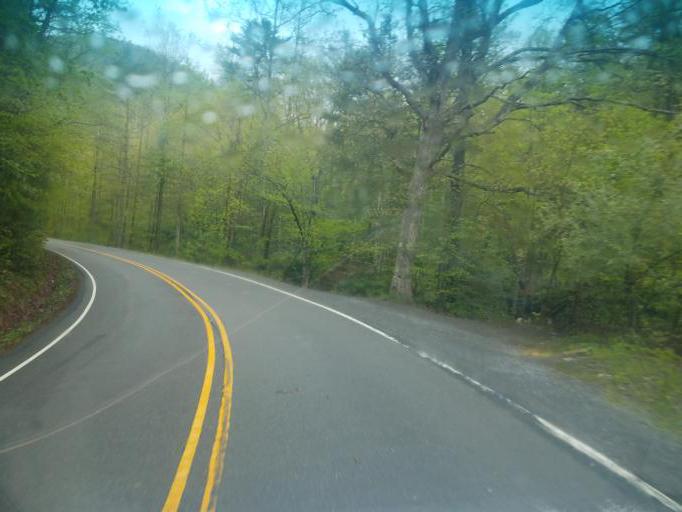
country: US
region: Tennessee
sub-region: Johnson County
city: Mountain City
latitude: 36.6260
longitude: -81.7558
